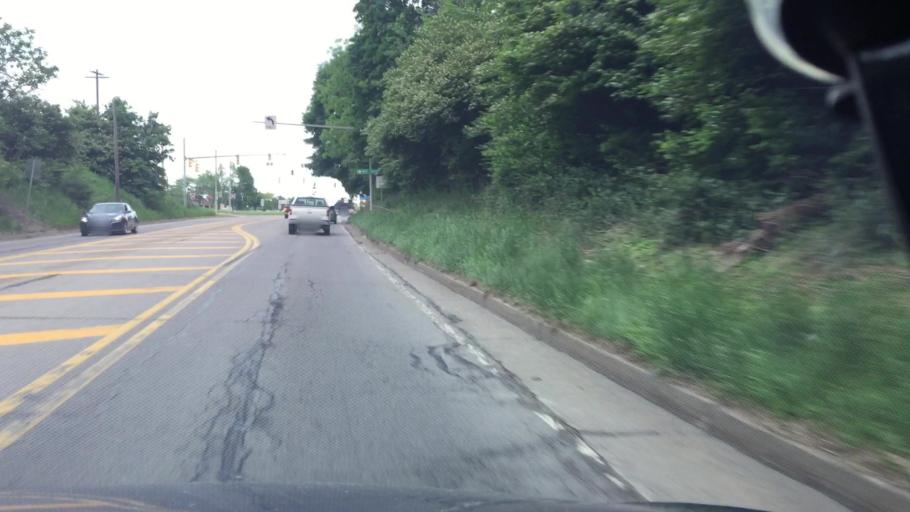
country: US
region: Pennsylvania
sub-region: Butler County
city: Shanor-Northvue
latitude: 40.9000
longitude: -79.9105
